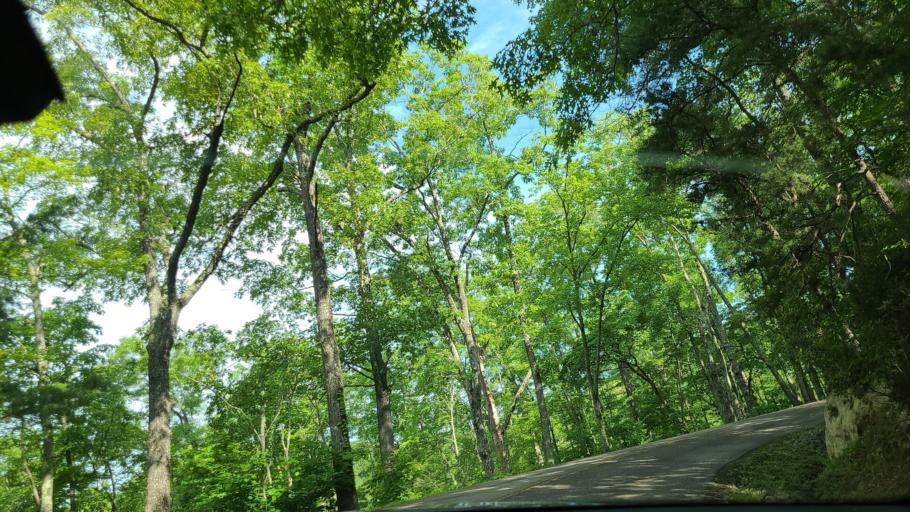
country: US
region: Kentucky
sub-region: Bell County
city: Pineville
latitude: 36.7464
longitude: -83.7143
